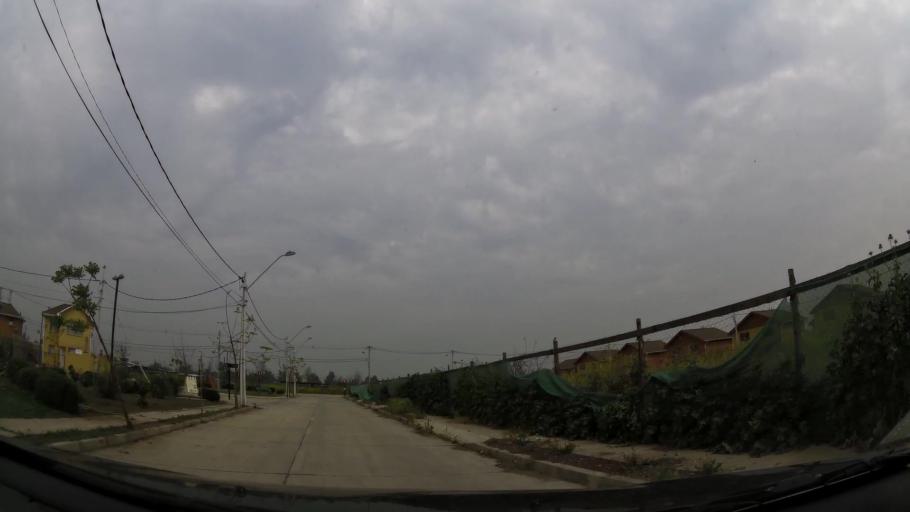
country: CL
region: Santiago Metropolitan
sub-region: Provincia de Chacabuco
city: Chicureo Abajo
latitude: -33.1925
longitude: -70.6821
